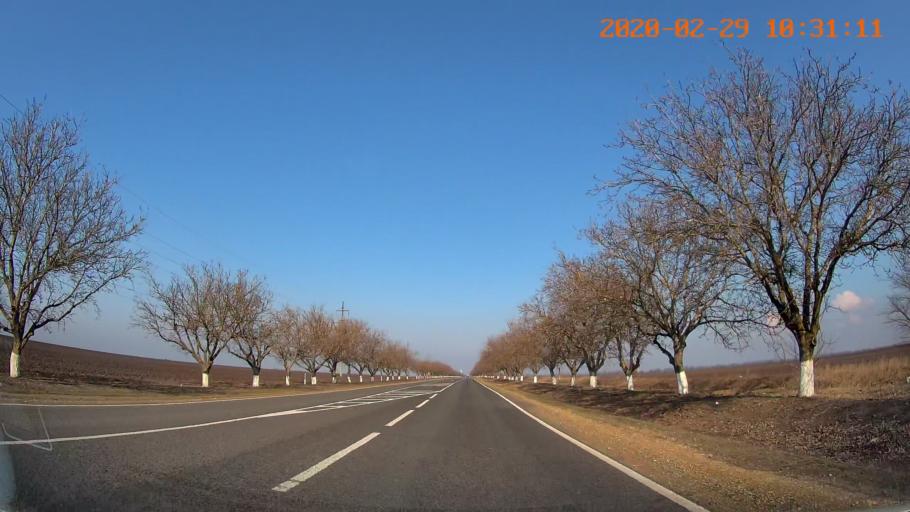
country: MD
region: Telenesti
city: Tiraspolul Nou
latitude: 46.9449
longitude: 29.5670
